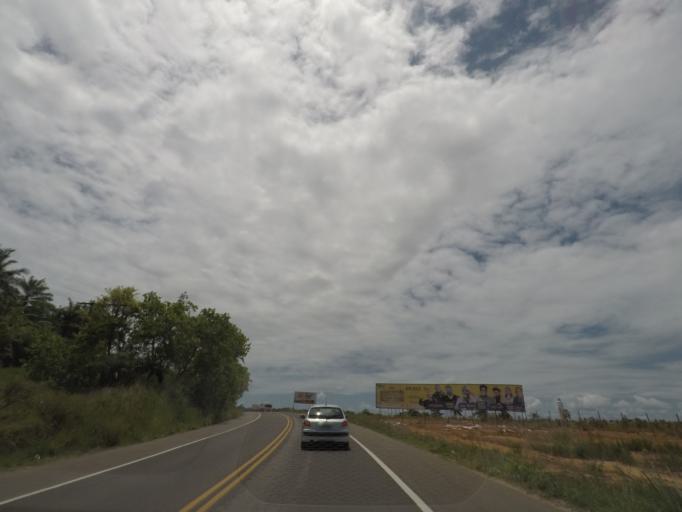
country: BR
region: Bahia
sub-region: Itaparica
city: Itaparica
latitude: -12.9414
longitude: -38.6312
